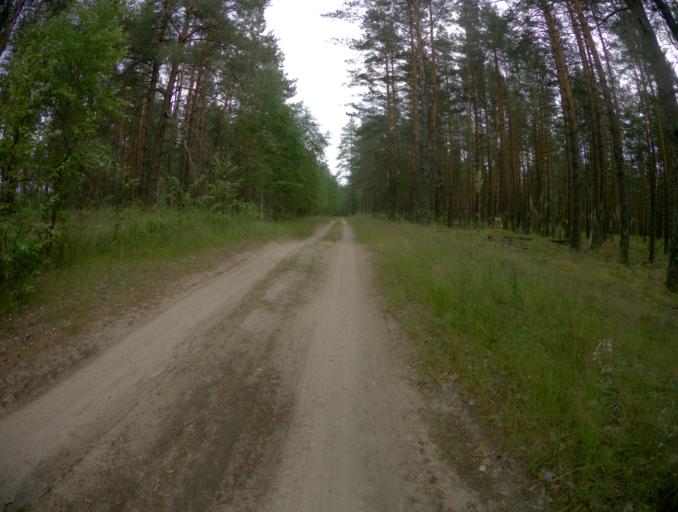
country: RU
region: Nizjnij Novgorod
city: Frolishchi
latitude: 56.3451
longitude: 42.7327
